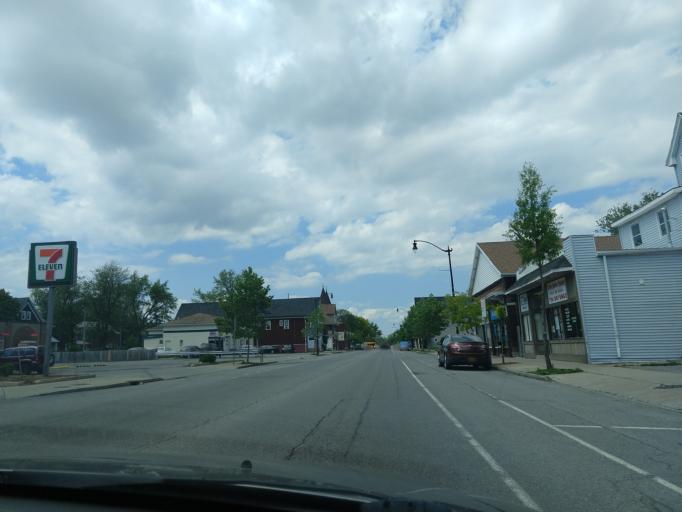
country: US
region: New York
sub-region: Erie County
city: Lackawanna
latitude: 42.8449
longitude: -78.8237
